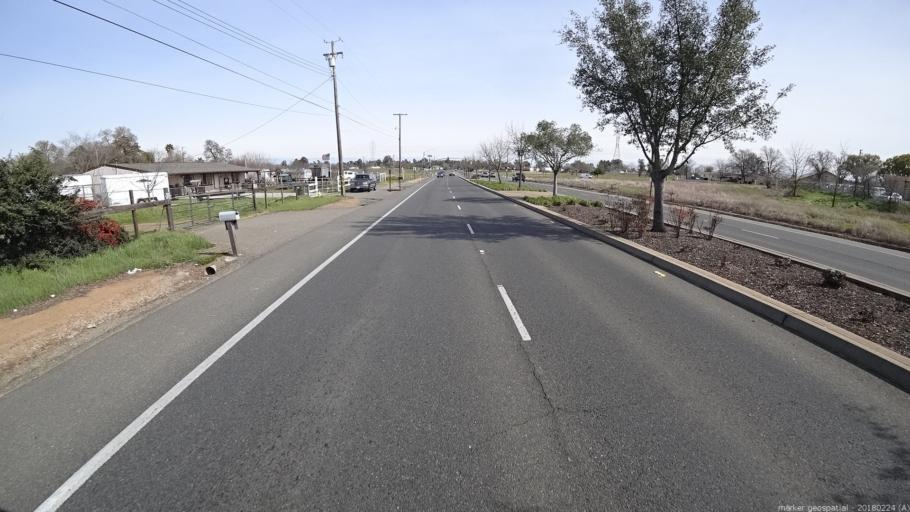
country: US
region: California
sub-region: Sacramento County
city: Rio Linda
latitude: 38.6874
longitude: -121.4307
